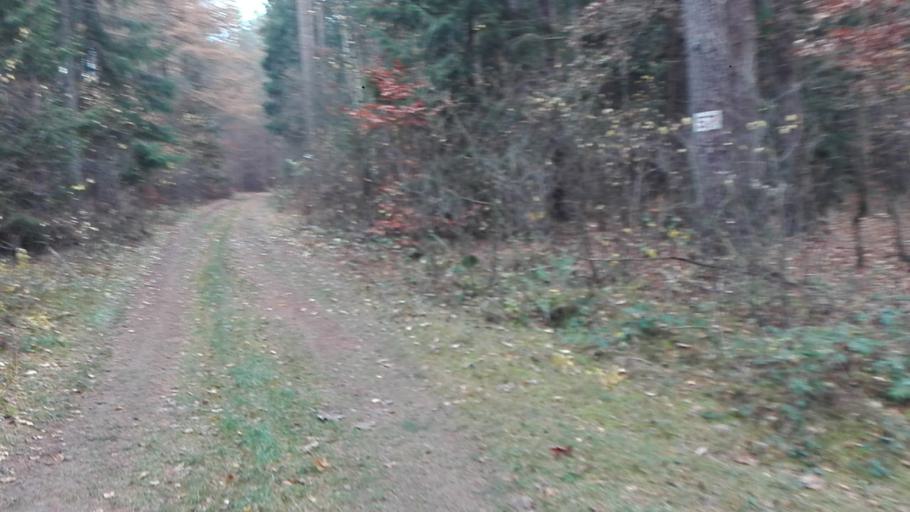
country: PL
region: West Pomeranian Voivodeship
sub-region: Powiat szczecinecki
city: Barwice
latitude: 53.8064
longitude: 16.3562
